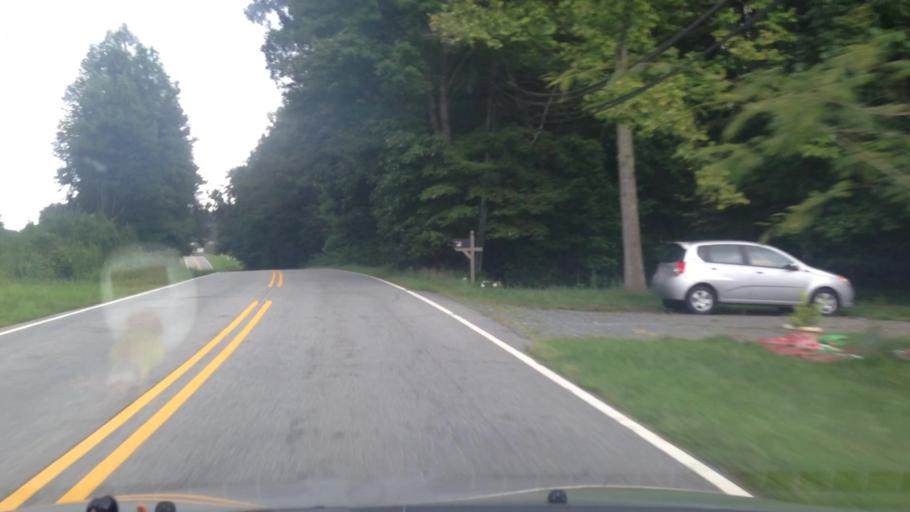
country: US
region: North Carolina
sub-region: Forsyth County
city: Walkertown
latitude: 36.1997
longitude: -80.1661
